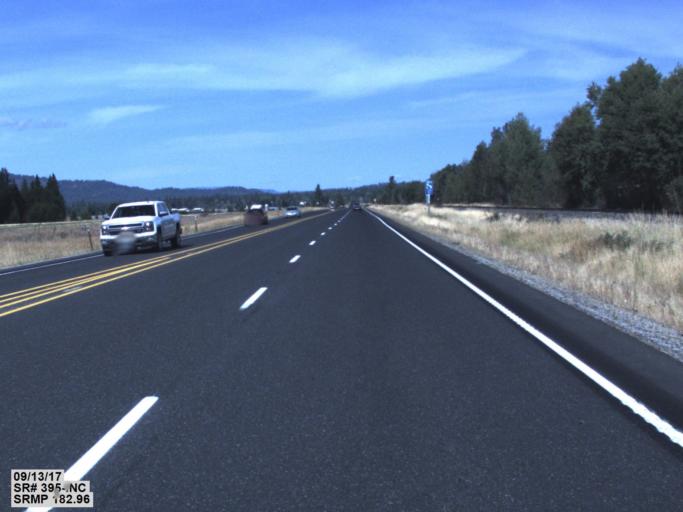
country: US
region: Washington
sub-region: Spokane County
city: Deer Park
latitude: 47.9799
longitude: -117.5256
